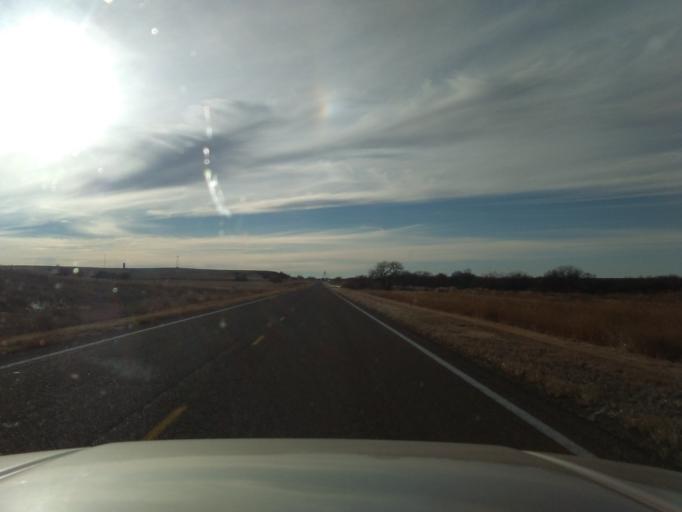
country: US
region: Kansas
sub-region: Norton County
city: Norton
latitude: 39.7461
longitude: -100.1565
